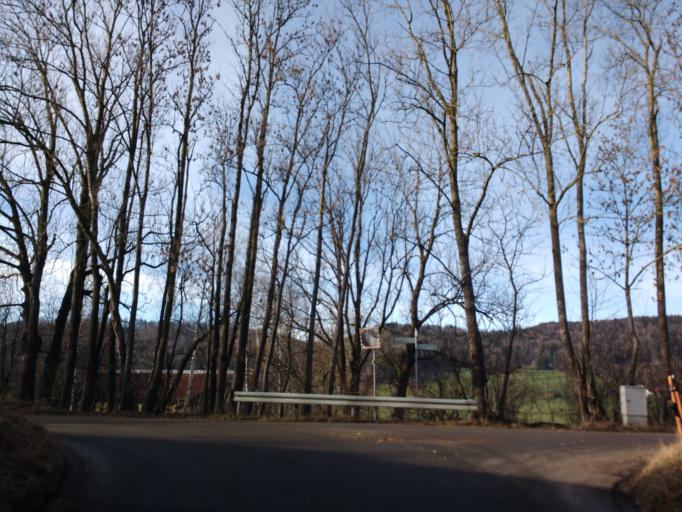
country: DE
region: Bavaria
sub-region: Swabia
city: Wildpoldsried
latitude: 47.7792
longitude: 10.4021
